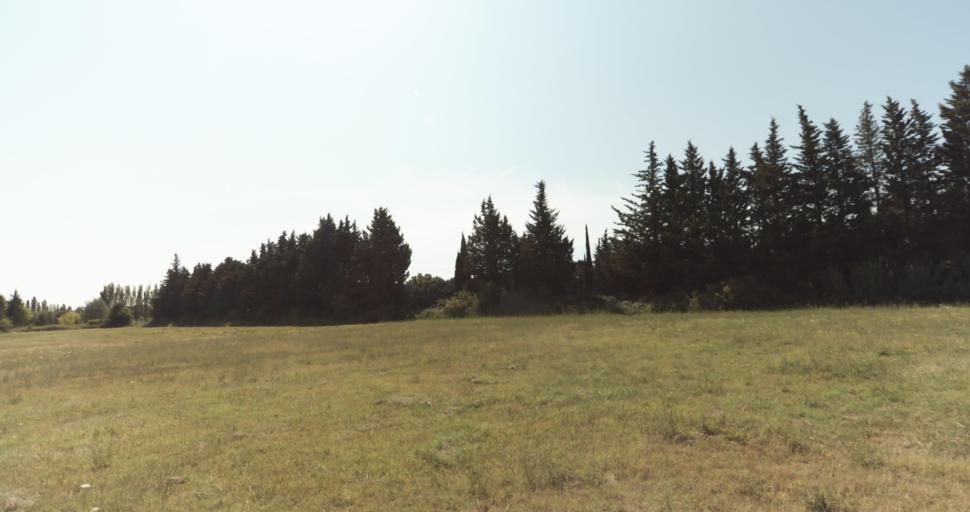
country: FR
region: Provence-Alpes-Cote d'Azur
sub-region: Departement du Vaucluse
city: Monteux
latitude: 44.0142
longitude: 4.9892
